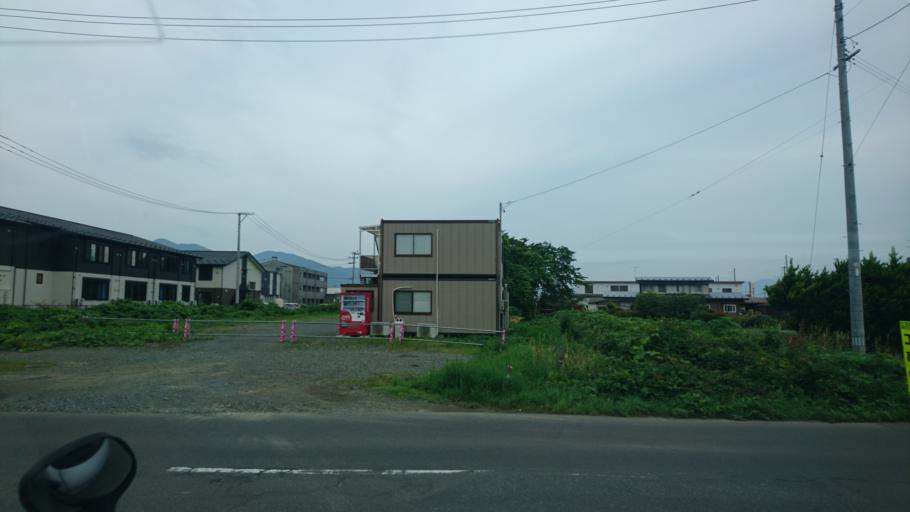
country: JP
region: Iwate
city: Morioka-shi
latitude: 39.6682
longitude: 141.1422
